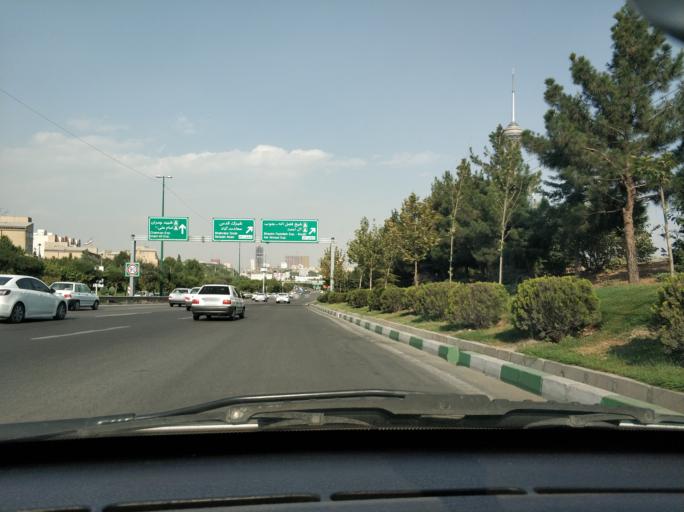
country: IR
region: Tehran
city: Tehran
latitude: 35.7493
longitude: 51.3631
